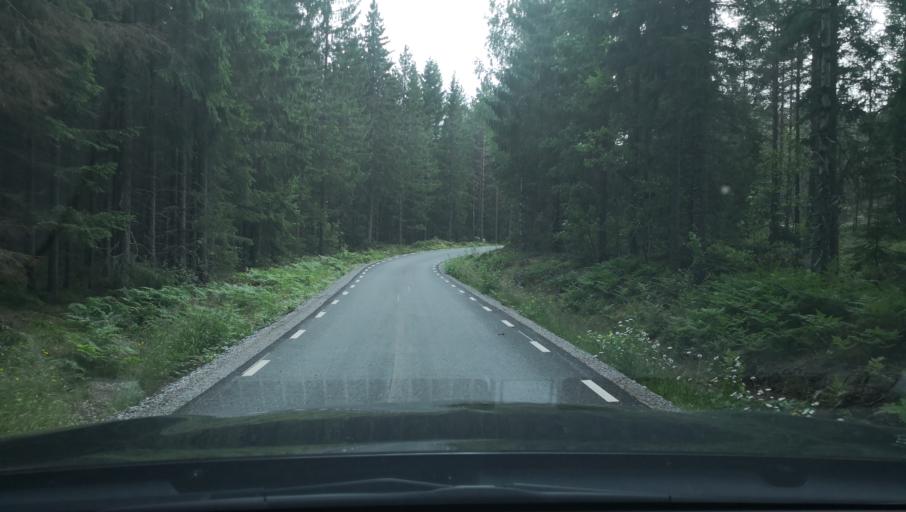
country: SE
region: Vaestmanland
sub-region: Surahammars Kommun
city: Surahammar
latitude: 59.6649
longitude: 16.1349
